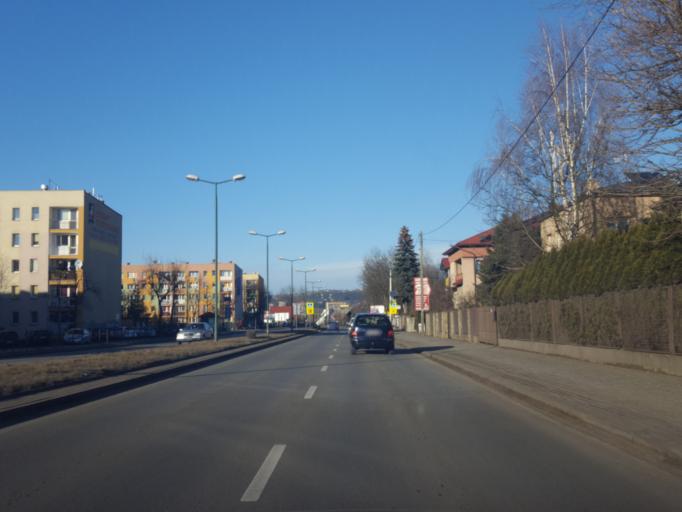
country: PL
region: Lesser Poland Voivodeship
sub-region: Powiat nowosadecki
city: Nowy Sacz
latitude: 49.6129
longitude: 20.7106
